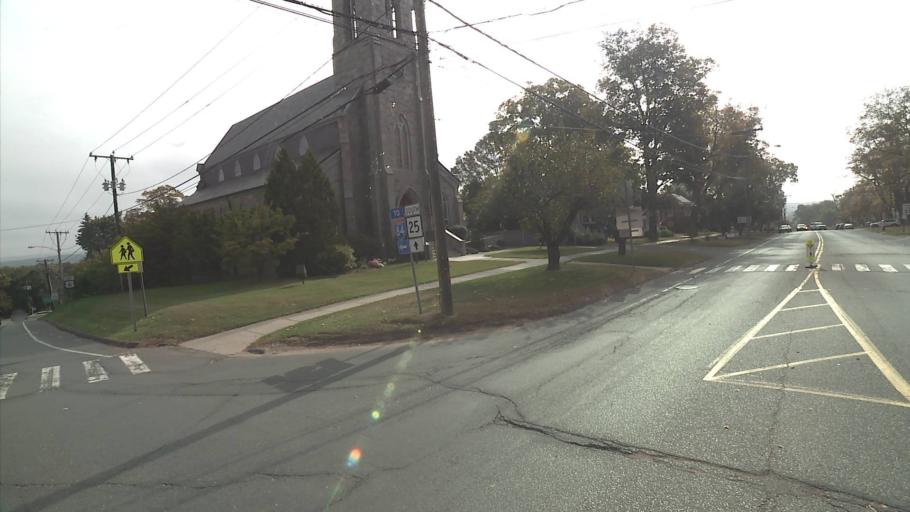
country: US
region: Connecticut
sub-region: Fairfield County
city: Newtown
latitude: 41.4135
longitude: -73.3088
